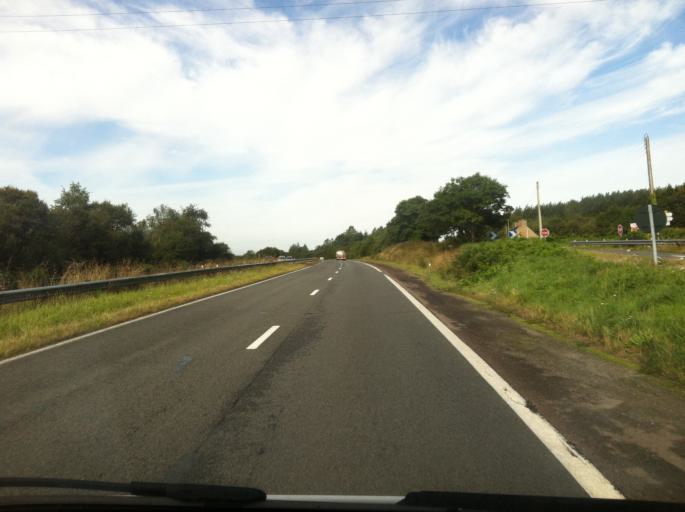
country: FR
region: Brittany
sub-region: Departement des Cotes-d'Armor
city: Louargat
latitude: 48.5671
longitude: -3.3171
